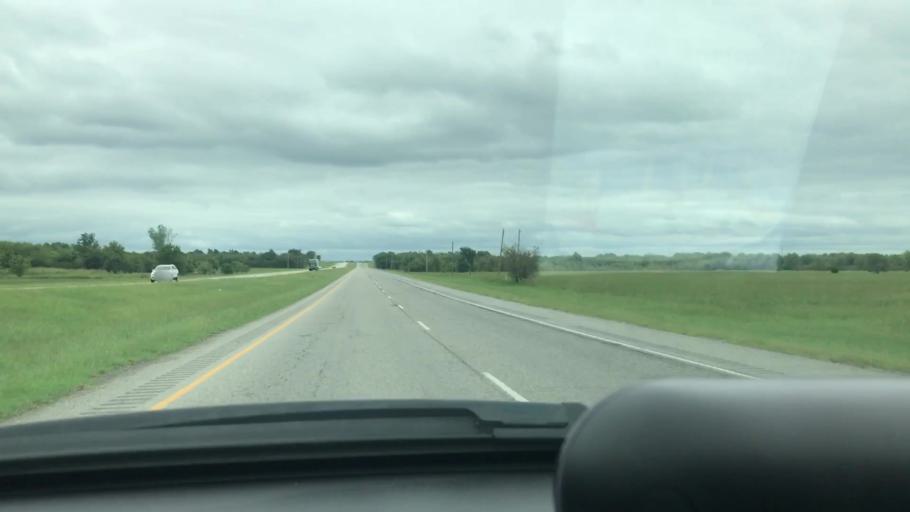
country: US
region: Oklahoma
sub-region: Wagoner County
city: Wagoner
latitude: 35.9828
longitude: -95.3783
